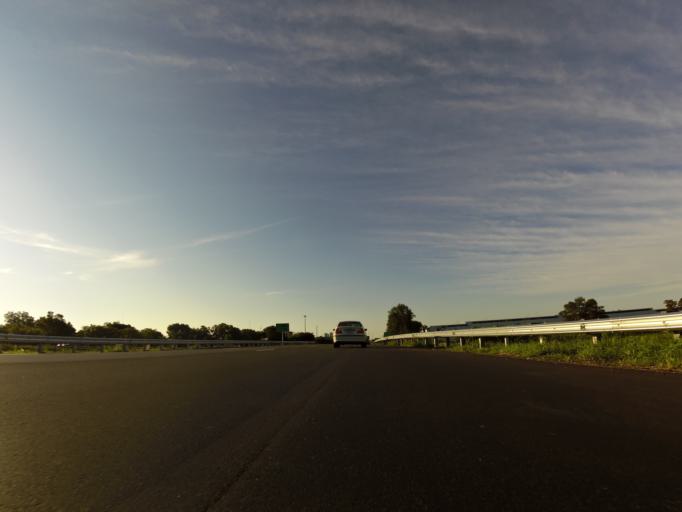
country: US
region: Kansas
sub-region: Sedgwick County
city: Park City
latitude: 37.7577
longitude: -97.3215
